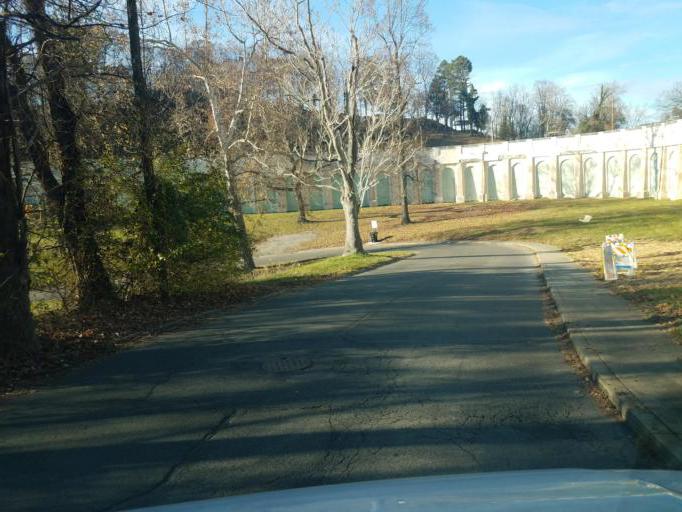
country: US
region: Ohio
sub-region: Scioto County
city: Portsmouth
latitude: 38.7531
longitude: -82.9862
